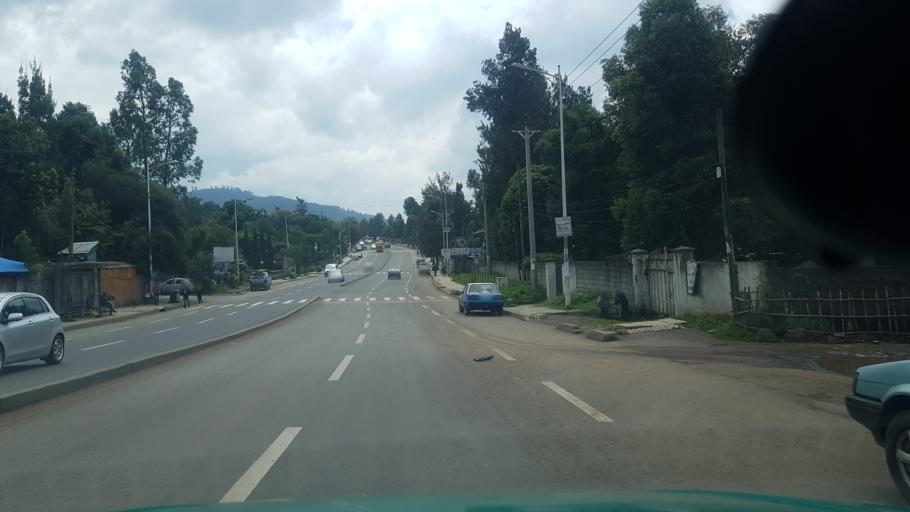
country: ET
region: Adis Abeba
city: Addis Ababa
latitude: 9.0204
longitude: 38.7711
